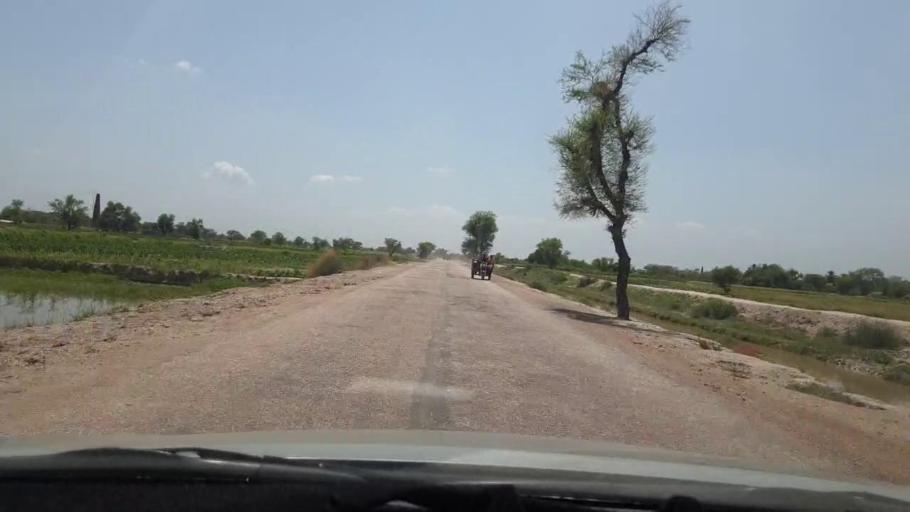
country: PK
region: Sindh
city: Pano Aqil
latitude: 27.7230
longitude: 69.1768
